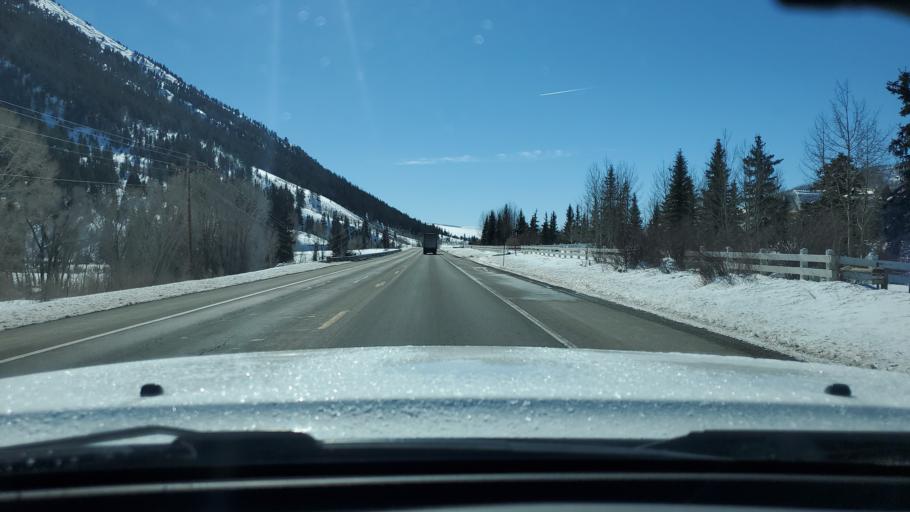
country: US
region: Colorado
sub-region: Gunnison County
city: Crested Butte
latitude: 38.7903
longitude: -106.8739
